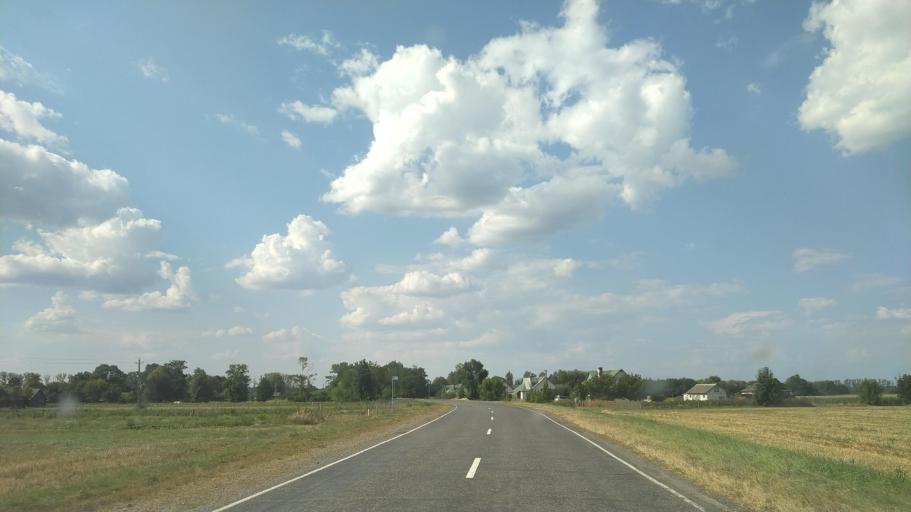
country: BY
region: Brest
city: Drahichyn
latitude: 52.2492
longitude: 25.0970
